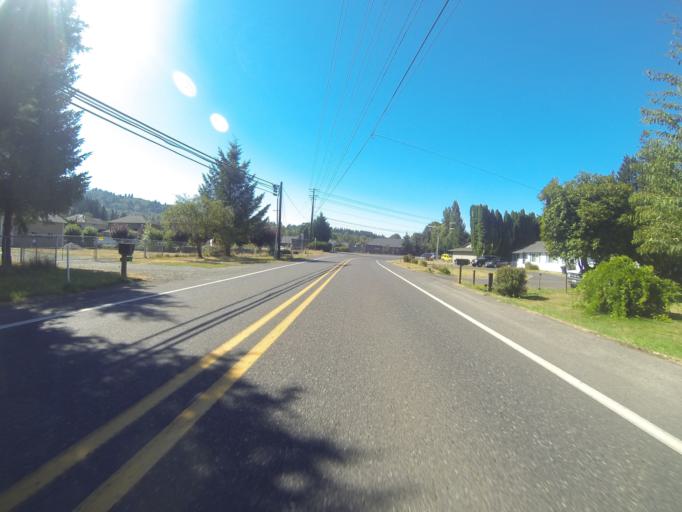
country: US
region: Washington
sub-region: Cowlitz County
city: Woodland
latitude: 45.9210
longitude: -122.7254
